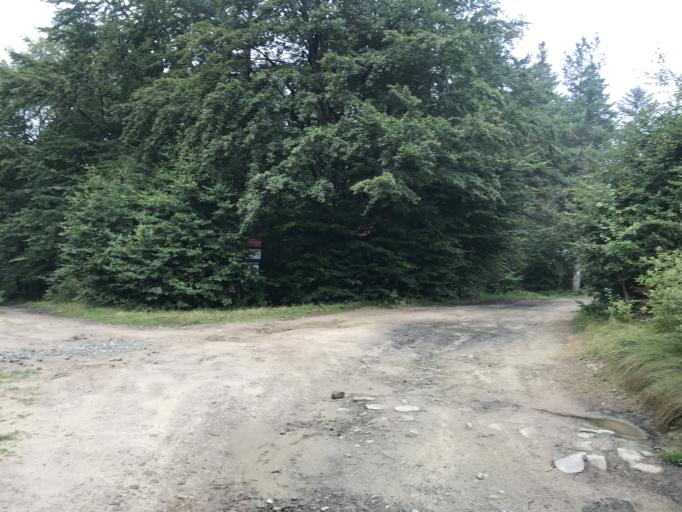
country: PL
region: Lesser Poland Voivodeship
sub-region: Powiat nowosadecki
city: Rytro
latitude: 49.4203
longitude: 20.6170
